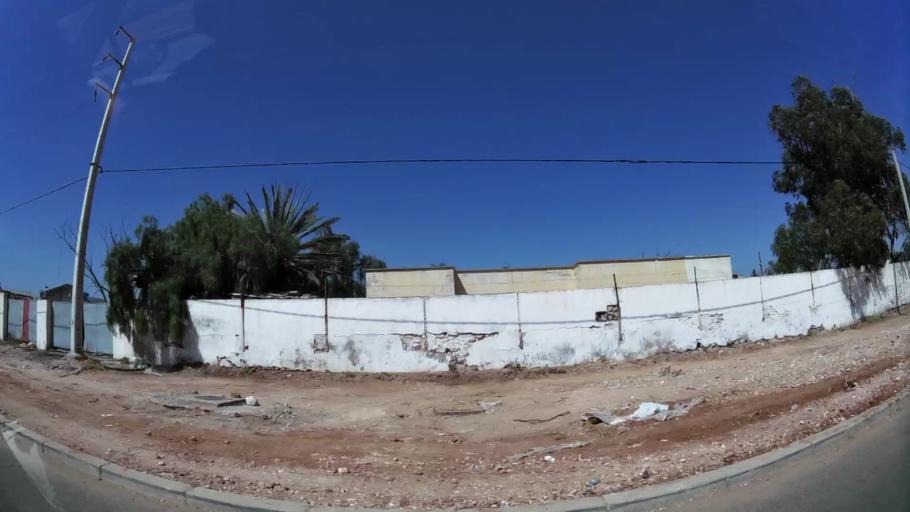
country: MA
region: Souss-Massa-Draa
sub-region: Agadir-Ida-ou-Tnan
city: Agadir
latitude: 30.4201
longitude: -9.5799
